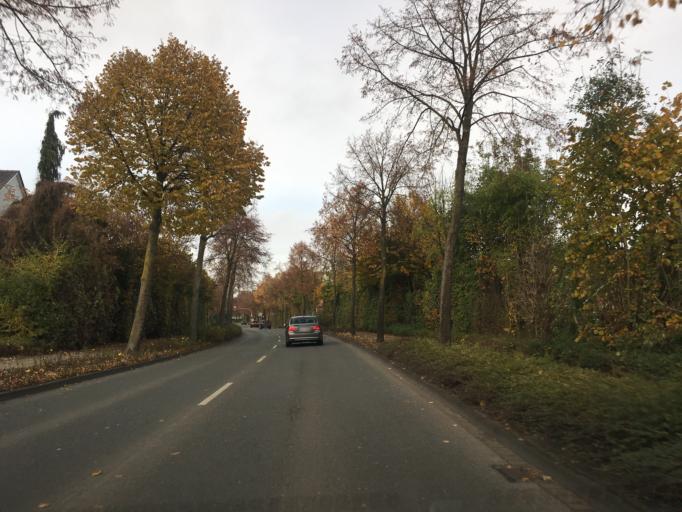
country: DE
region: North Rhine-Westphalia
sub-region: Regierungsbezirk Munster
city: Steinfurt
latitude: 52.1231
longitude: 7.3904
